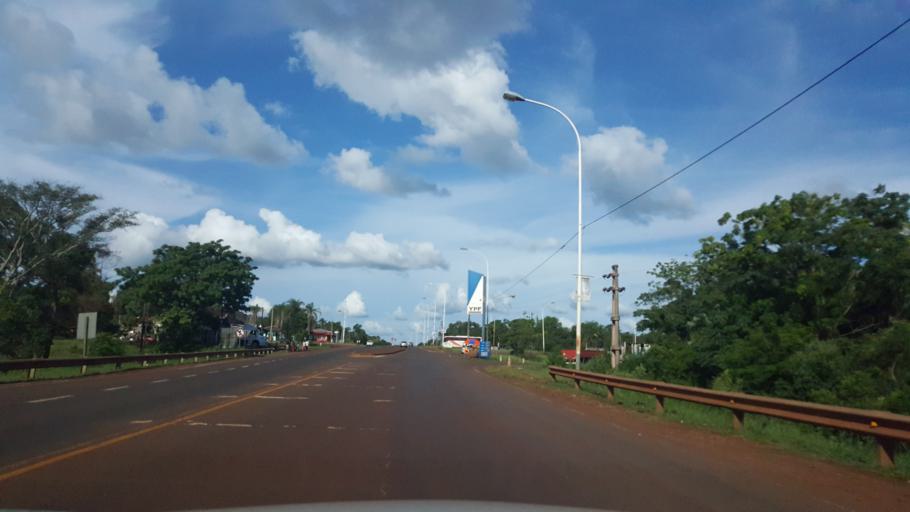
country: AR
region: Misiones
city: Santa Ana
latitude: -27.3780
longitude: -55.5778
